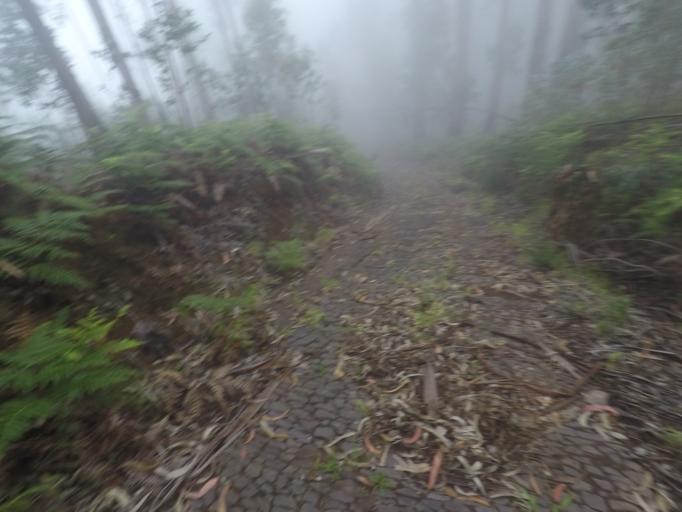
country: PT
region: Madeira
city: Ponta do Sol
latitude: 32.7151
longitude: -17.0940
